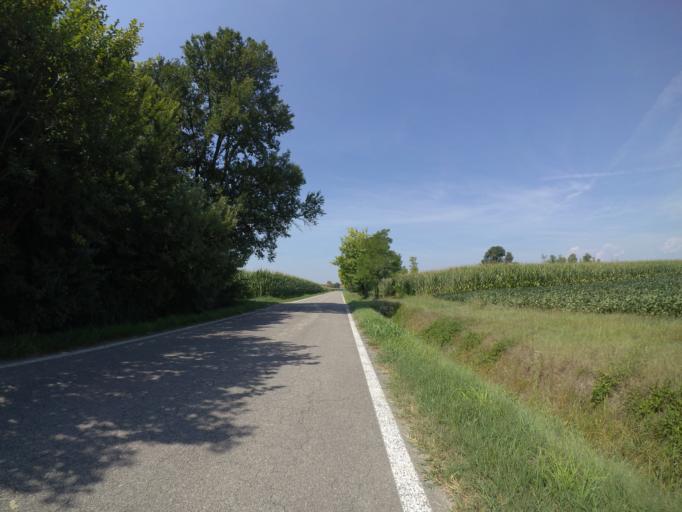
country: IT
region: Friuli Venezia Giulia
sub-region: Provincia di Udine
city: Varmo
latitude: 45.9008
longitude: 12.9743
